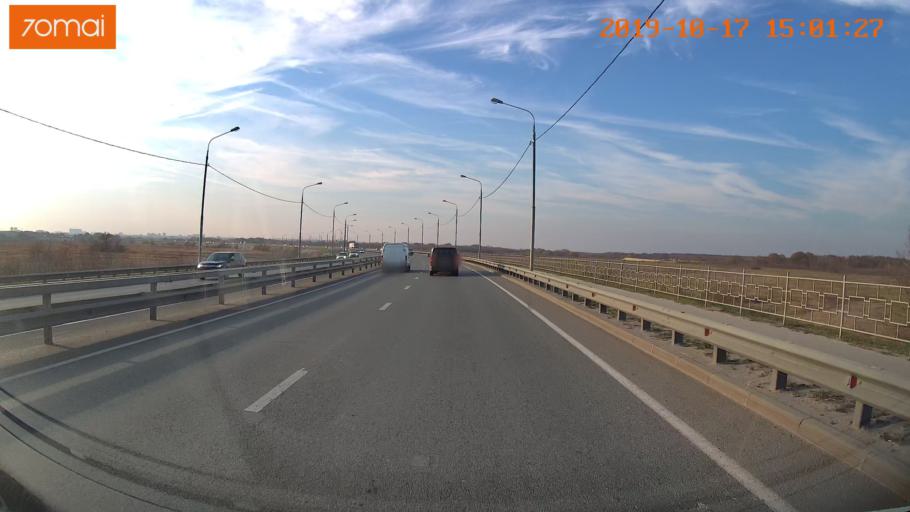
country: RU
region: Rjazan
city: Ryazan'
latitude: 54.6467
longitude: 39.7565
